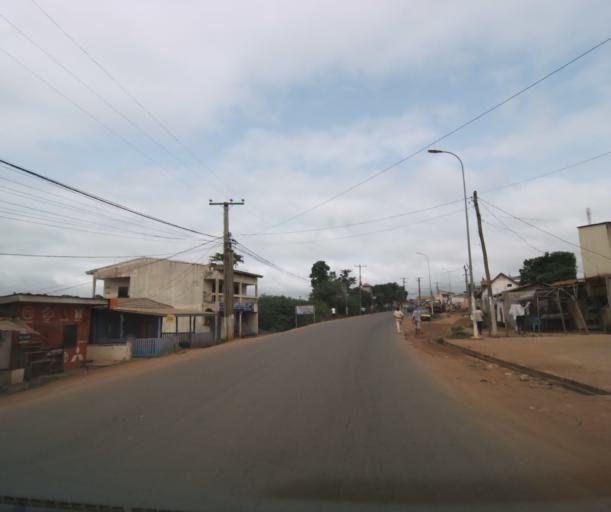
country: CM
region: Centre
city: Yaounde
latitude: 3.8012
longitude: 11.5286
